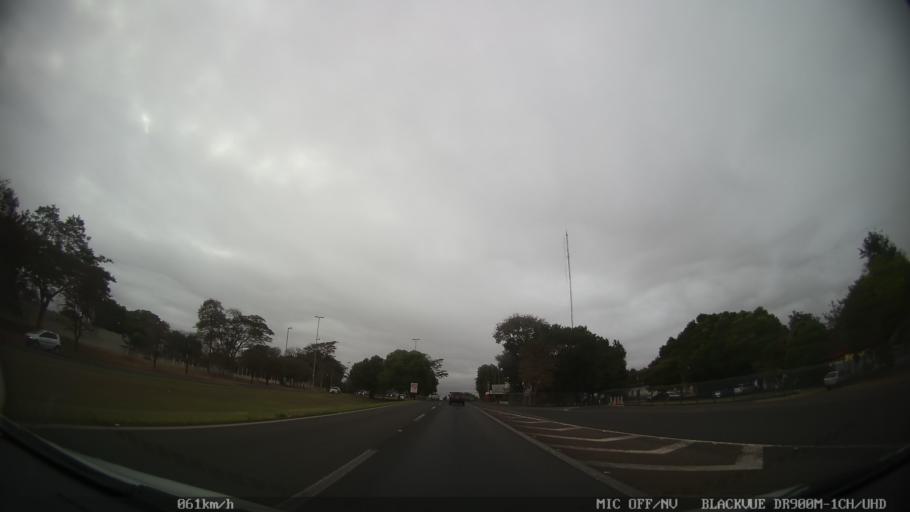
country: BR
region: Sao Paulo
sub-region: Sao Jose Do Rio Preto
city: Sao Jose do Rio Preto
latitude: -20.8224
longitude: -49.4228
